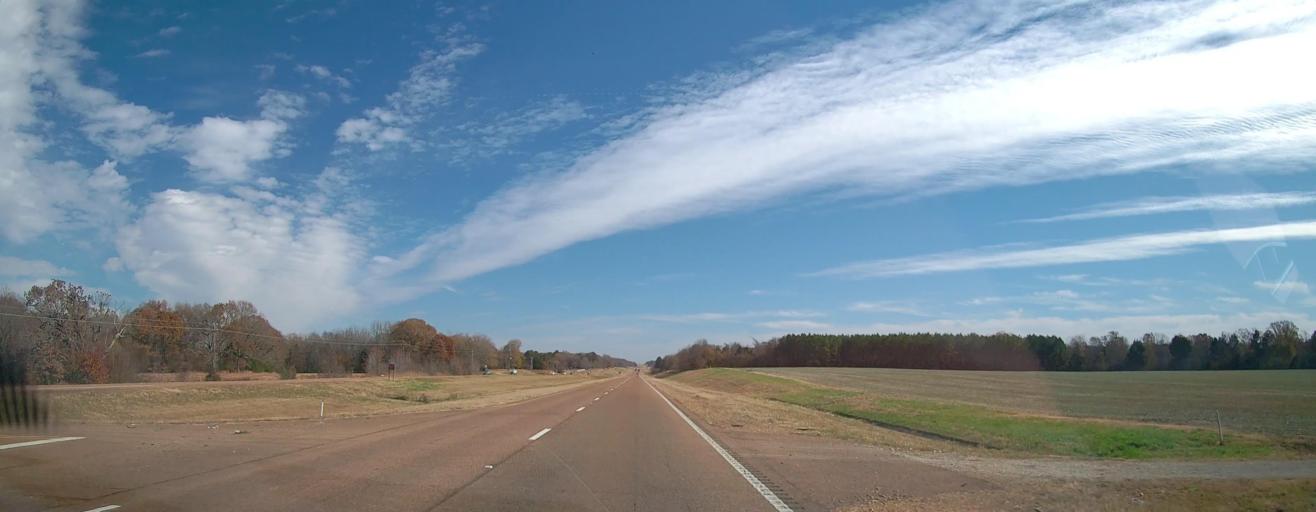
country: US
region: Mississippi
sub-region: Marshall County
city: Holly Springs
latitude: 34.9460
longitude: -89.3647
